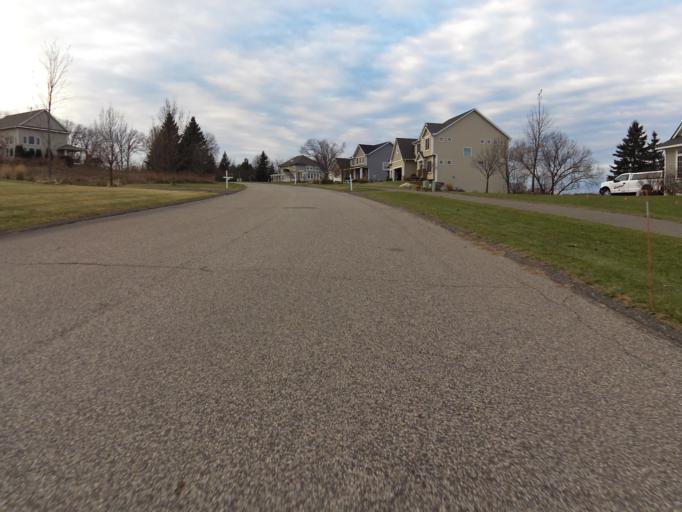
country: US
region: Minnesota
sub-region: Washington County
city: Oak Park Heights
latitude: 45.0115
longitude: -92.8002
